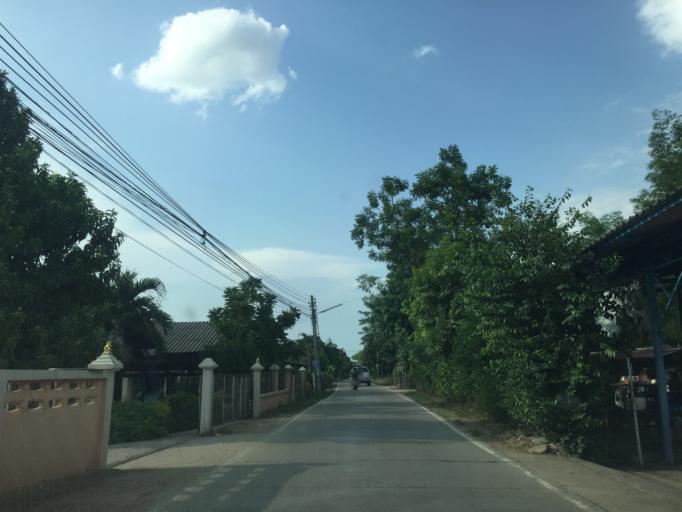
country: TH
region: Lamphun
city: Ban Thi
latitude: 18.6351
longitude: 99.0535
